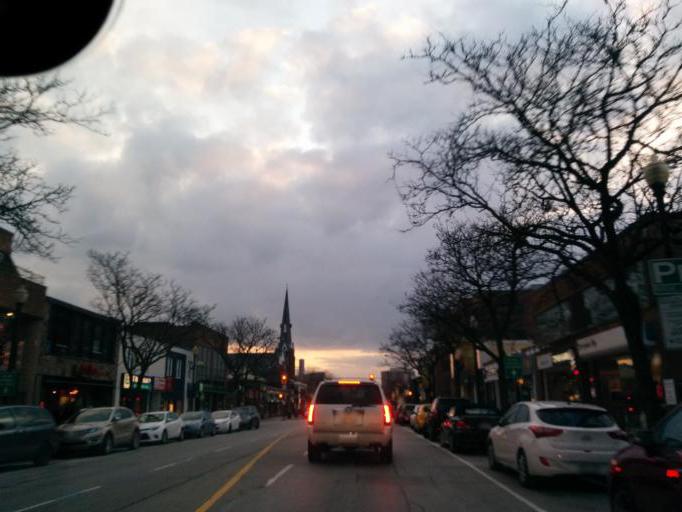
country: CA
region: Ontario
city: Oakville
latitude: 43.4480
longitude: -79.6658
